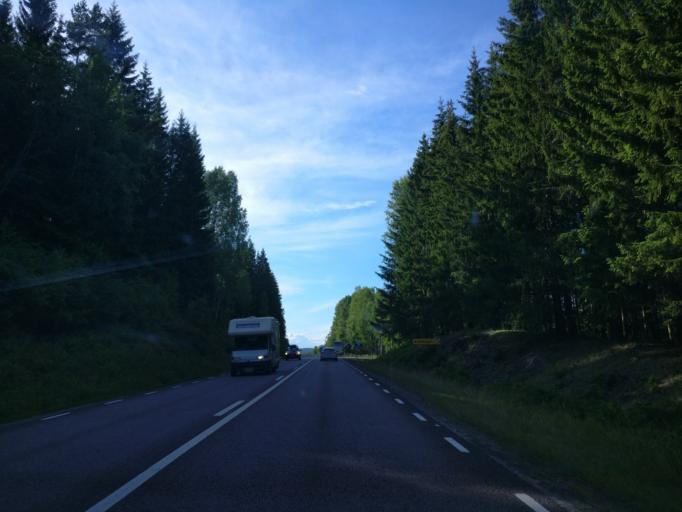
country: SE
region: Vaermland
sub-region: Karlstads Kommun
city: Edsvalla
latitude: 59.5479
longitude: 13.0616
